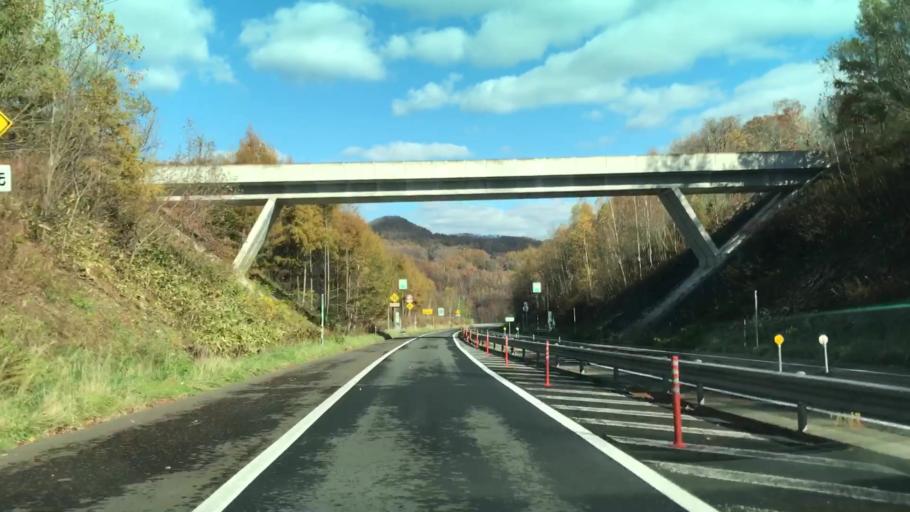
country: JP
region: Hokkaido
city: Chitose
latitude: 42.9121
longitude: 141.9089
